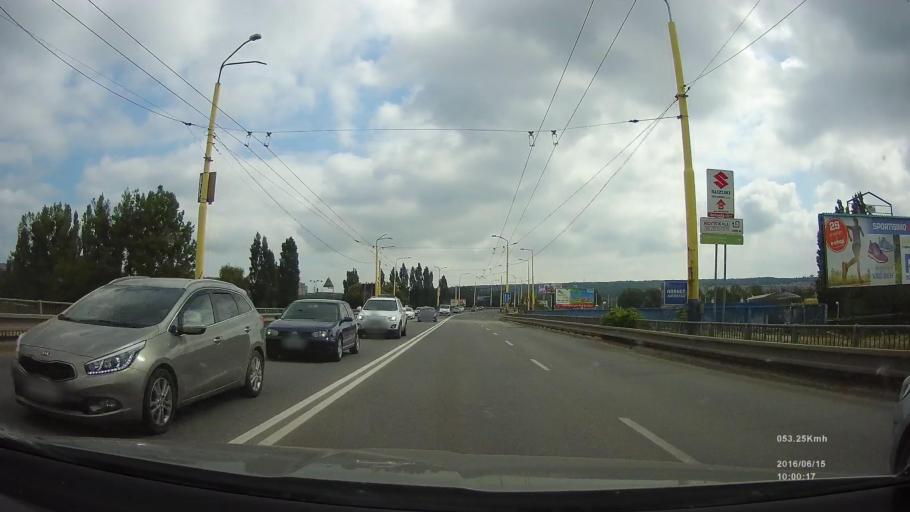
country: SK
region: Kosicky
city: Kosice
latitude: 48.7411
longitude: 21.2574
